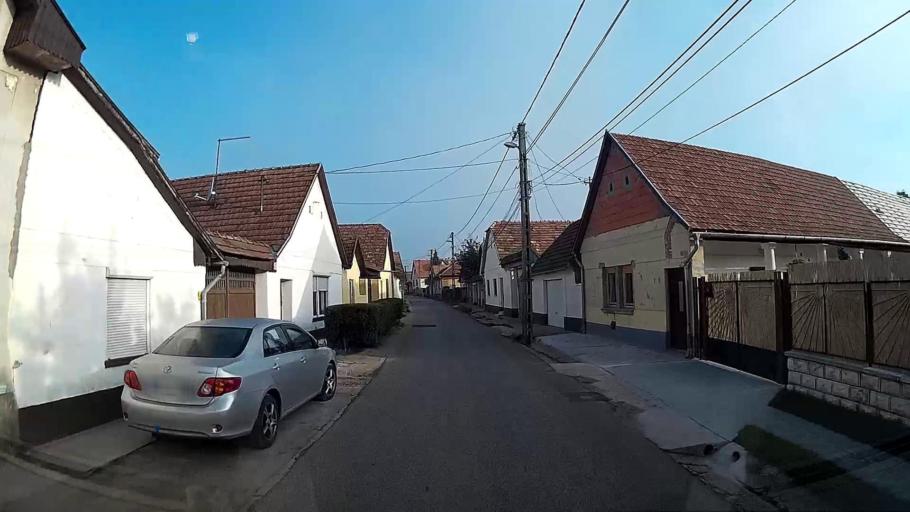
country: HU
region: Pest
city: Tahitotfalu
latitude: 47.7516
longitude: 19.0941
